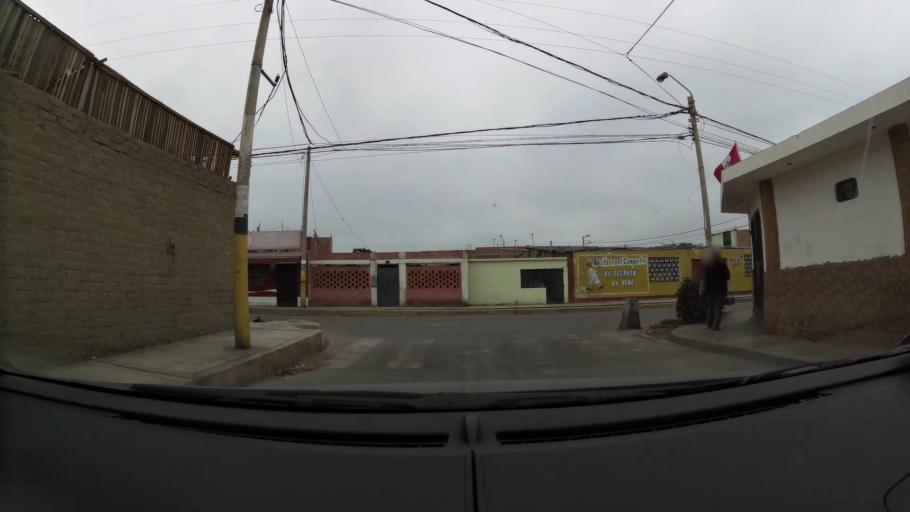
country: PE
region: Lima
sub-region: Barranca
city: Barranca
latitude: -10.7521
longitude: -77.7535
